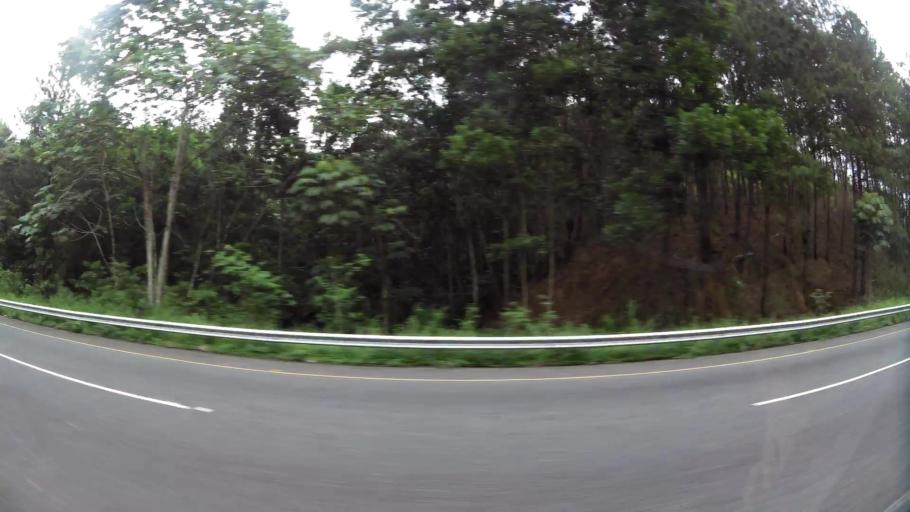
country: DO
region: Monsenor Nouel
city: Piedra Blanca
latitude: 18.8019
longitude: -70.2776
